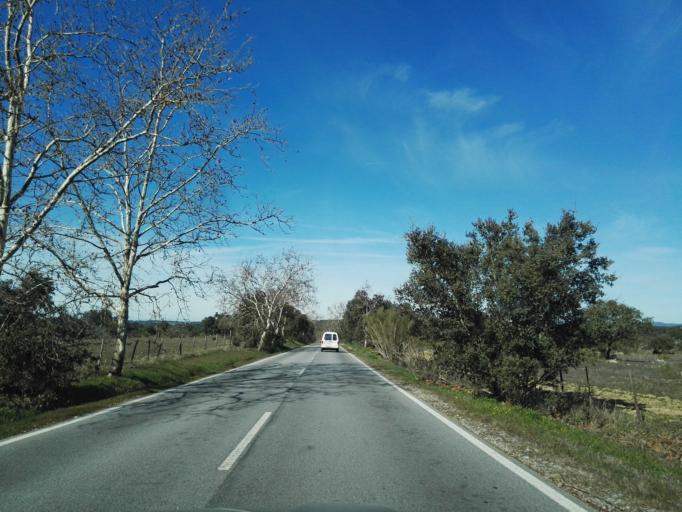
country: PT
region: Portalegre
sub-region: Arronches
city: Arronches
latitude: 39.0474
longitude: -7.2641
